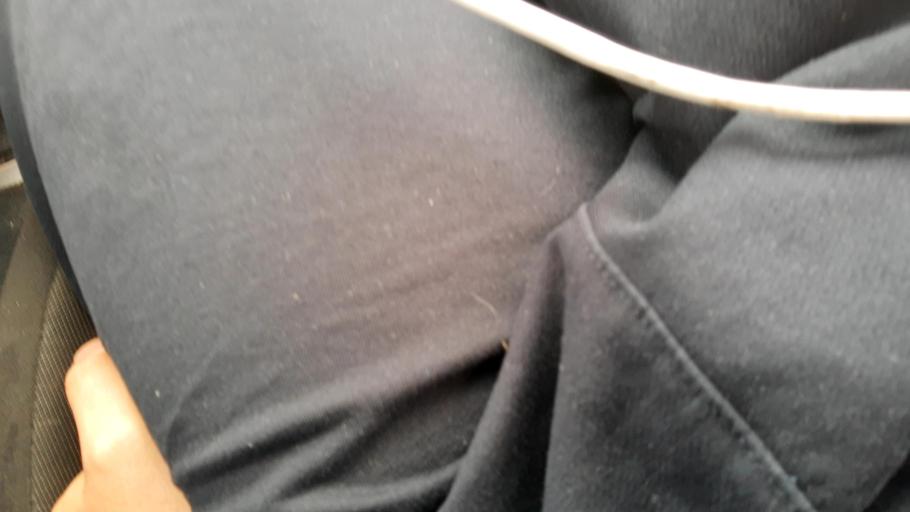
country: RU
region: Bashkortostan
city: Pavlovka
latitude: 55.3985
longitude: 56.4498
